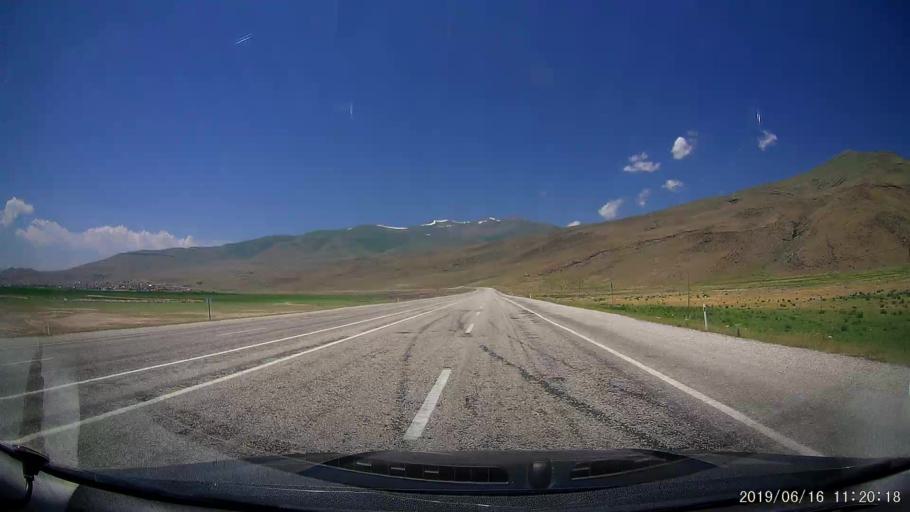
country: TR
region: Agri
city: Dogubayazit
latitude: 39.6982
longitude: 44.0937
